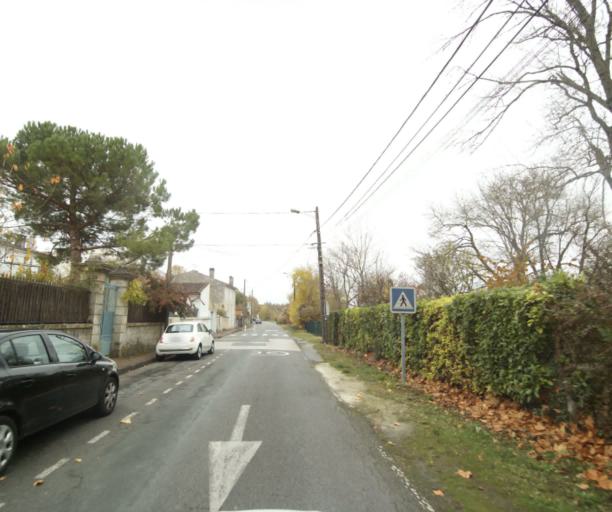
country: FR
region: Poitou-Charentes
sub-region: Departement de la Charente-Maritime
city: Saintes
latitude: 45.7290
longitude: -0.6389
